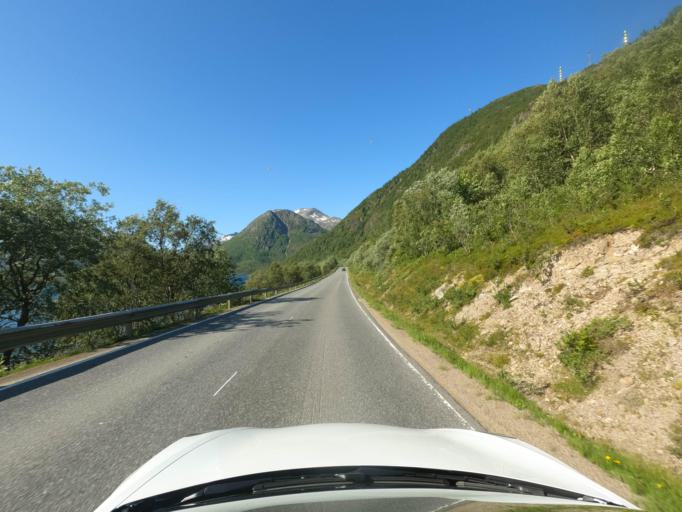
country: NO
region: Nordland
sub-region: Lodingen
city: Lodingen
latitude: 68.5630
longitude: 15.7943
